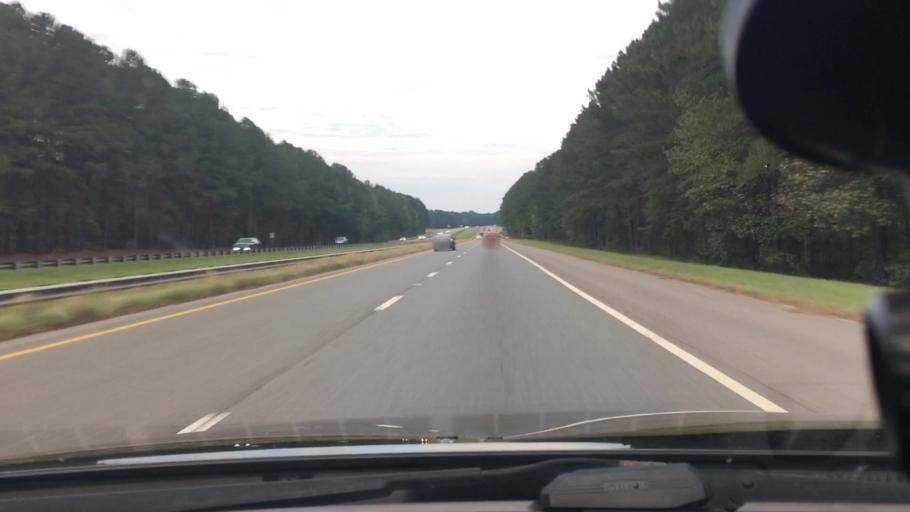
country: US
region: North Carolina
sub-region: Chatham County
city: Farmville
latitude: 35.5537
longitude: -79.1590
